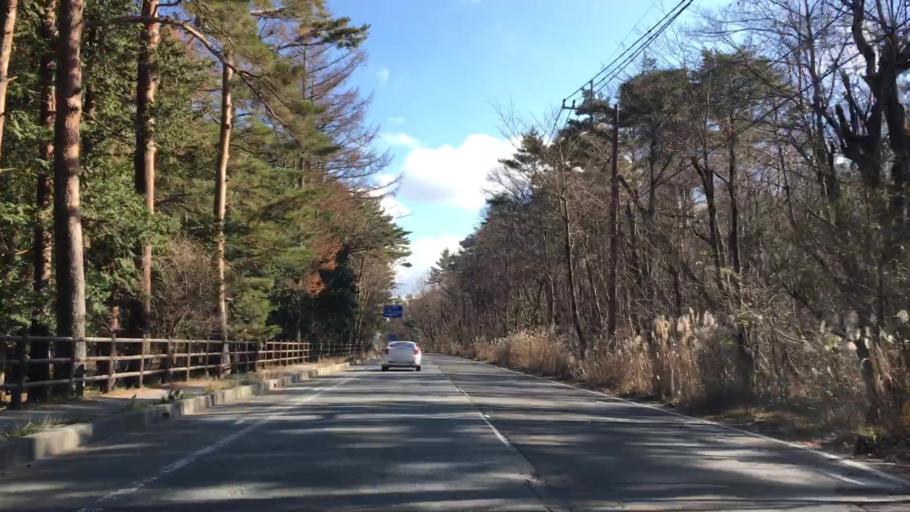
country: JP
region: Yamanashi
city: Fujikawaguchiko
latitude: 35.4456
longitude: 138.8240
